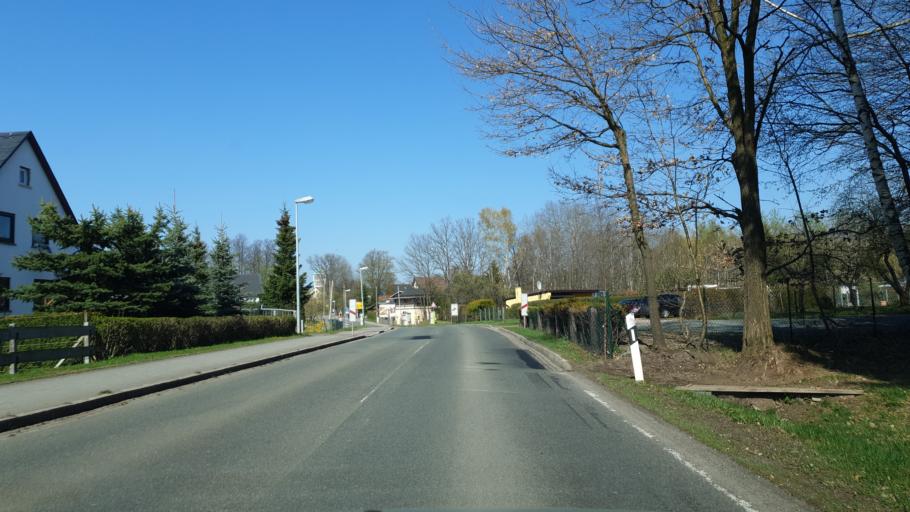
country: DE
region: Saxony
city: Oelsnitz
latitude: 50.7186
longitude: 12.7230
